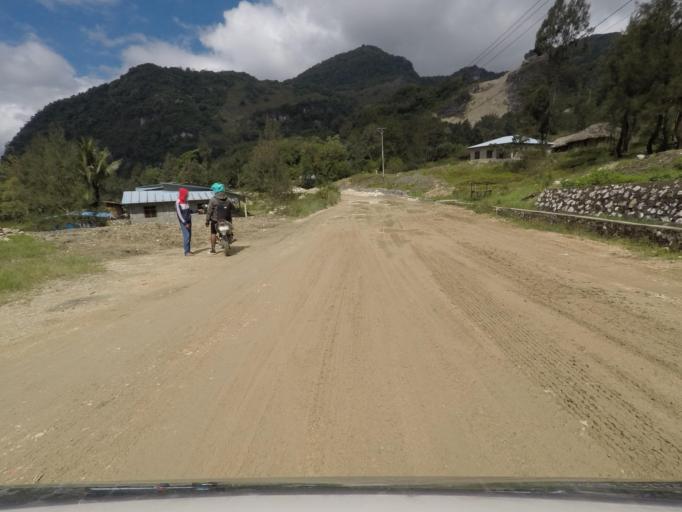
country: TL
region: Baucau
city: Venilale
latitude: -8.7091
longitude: 126.3642
